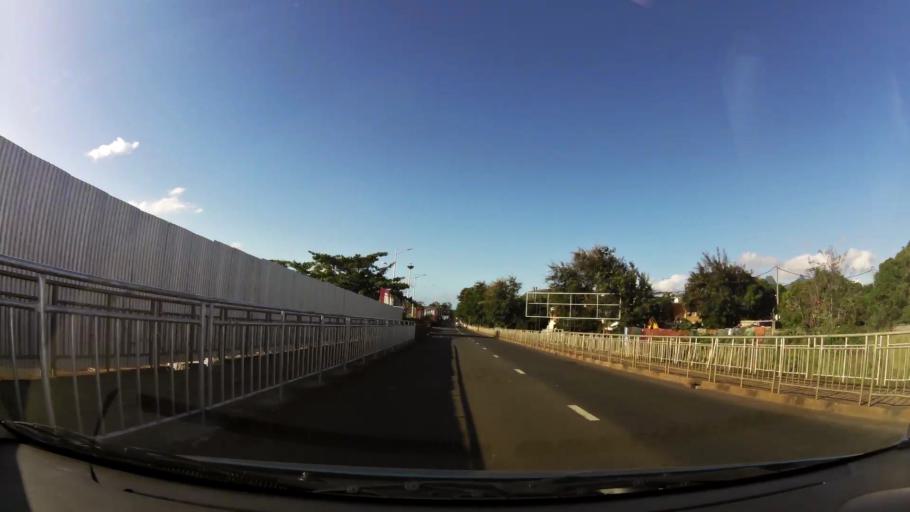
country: MU
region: Black River
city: Petite Riviere
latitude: -20.1889
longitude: 57.4561
